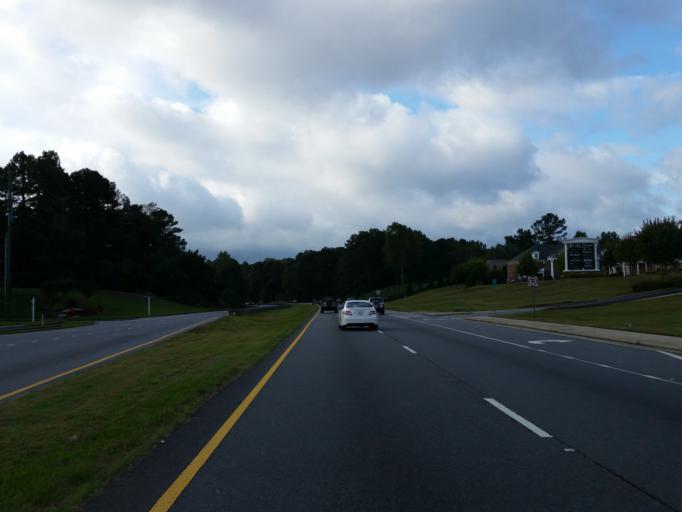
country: US
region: Georgia
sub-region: Cobb County
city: Acworth
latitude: 34.0506
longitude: -84.7011
